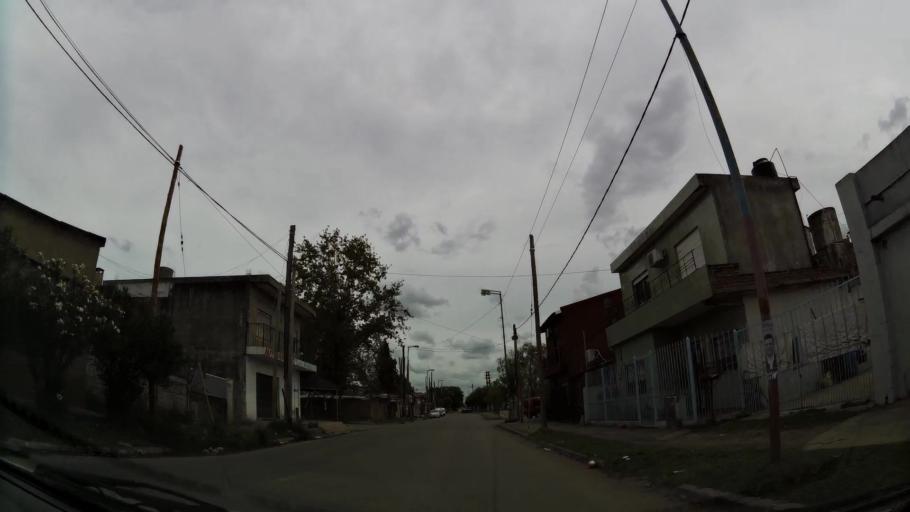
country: AR
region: Buenos Aires
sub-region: Partido de Quilmes
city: Quilmes
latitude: -34.7634
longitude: -58.2622
